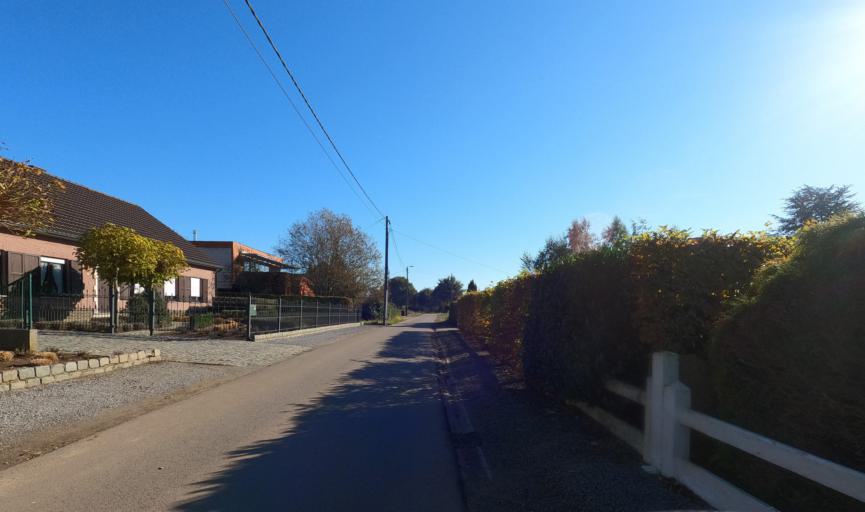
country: BE
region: Flanders
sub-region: Provincie Antwerpen
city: Heist-op-den-Berg
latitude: 51.1040
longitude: 4.7456
